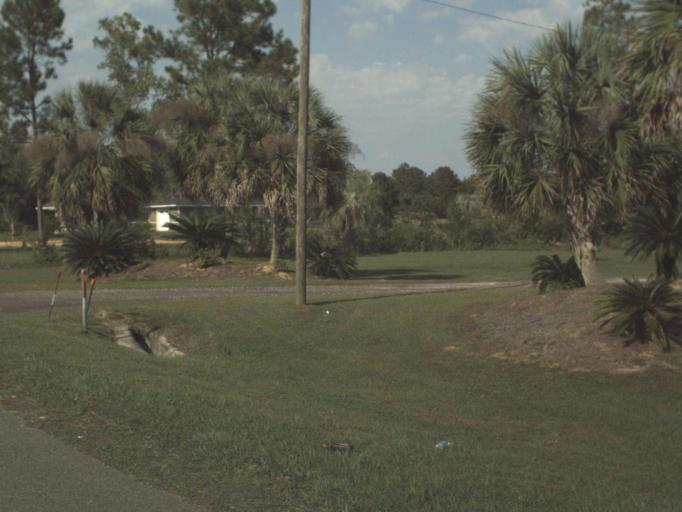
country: US
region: Florida
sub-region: Gulf County
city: Wewahitchka
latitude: 30.1356
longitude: -85.2085
